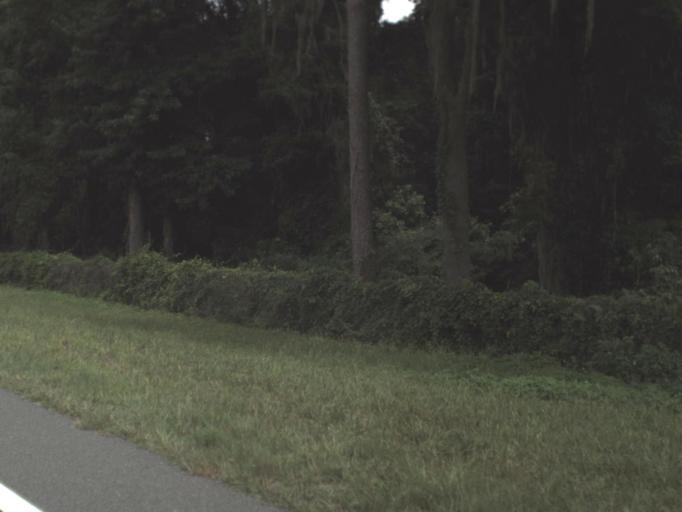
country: US
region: Florida
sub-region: Alachua County
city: Alachua
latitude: 29.8126
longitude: -82.4660
